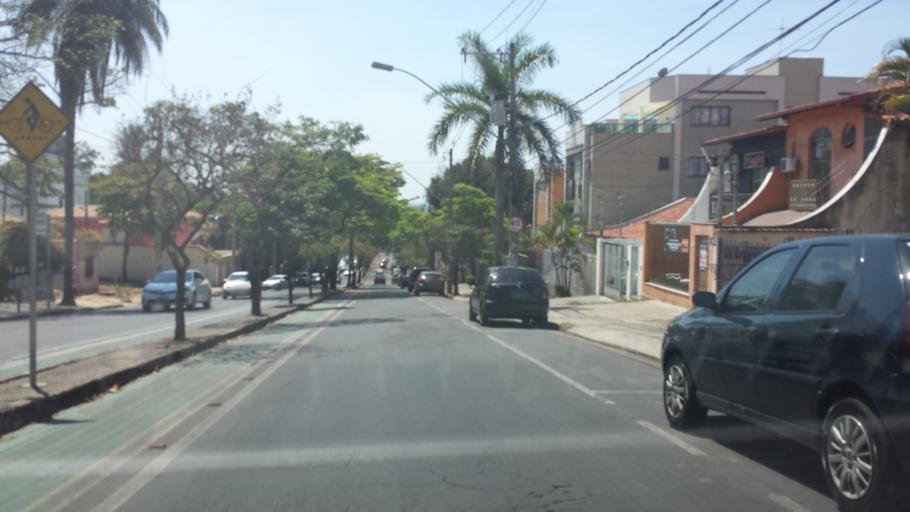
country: BR
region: Minas Gerais
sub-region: Belo Horizonte
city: Belo Horizonte
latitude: -19.8737
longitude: -43.9876
